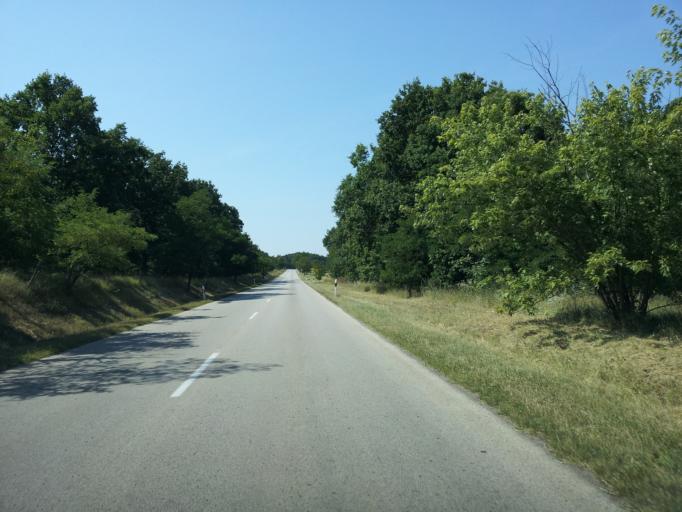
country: HU
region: Fejer
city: Pakozd
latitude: 47.2452
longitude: 18.5103
